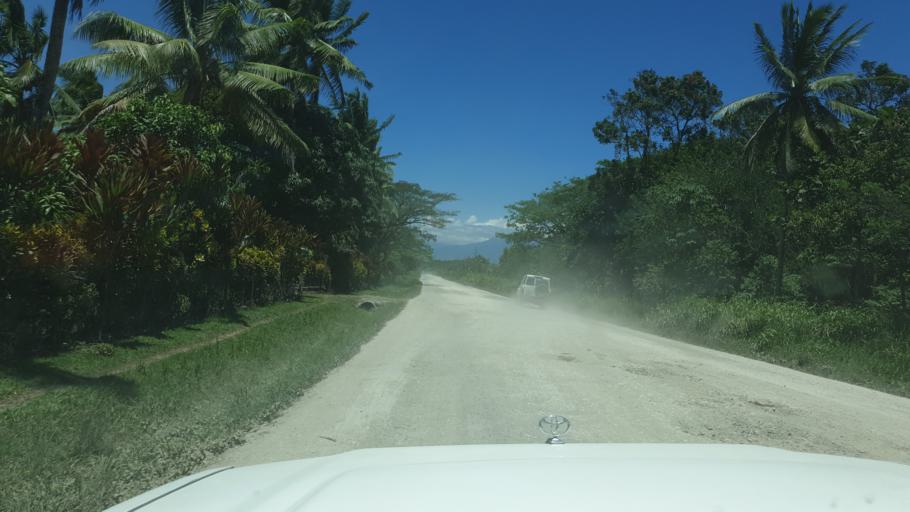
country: PG
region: Eastern Highlands
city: Goroka
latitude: -5.6744
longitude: 145.5006
